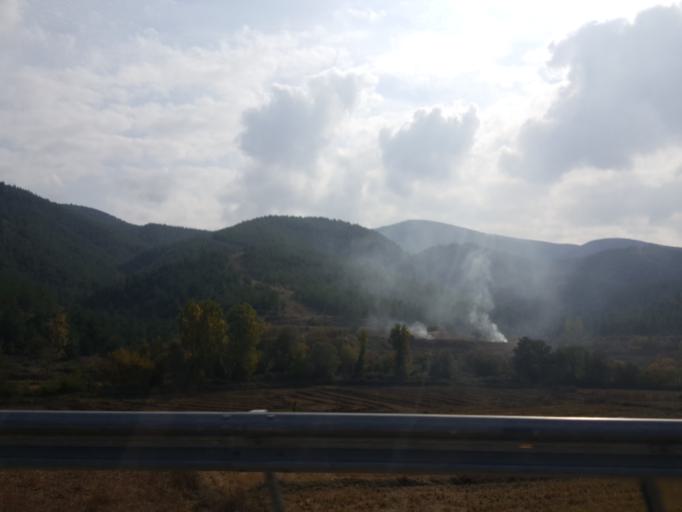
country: TR
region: Sinop
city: Sarayduzu
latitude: 41.3853
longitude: 34.9323
